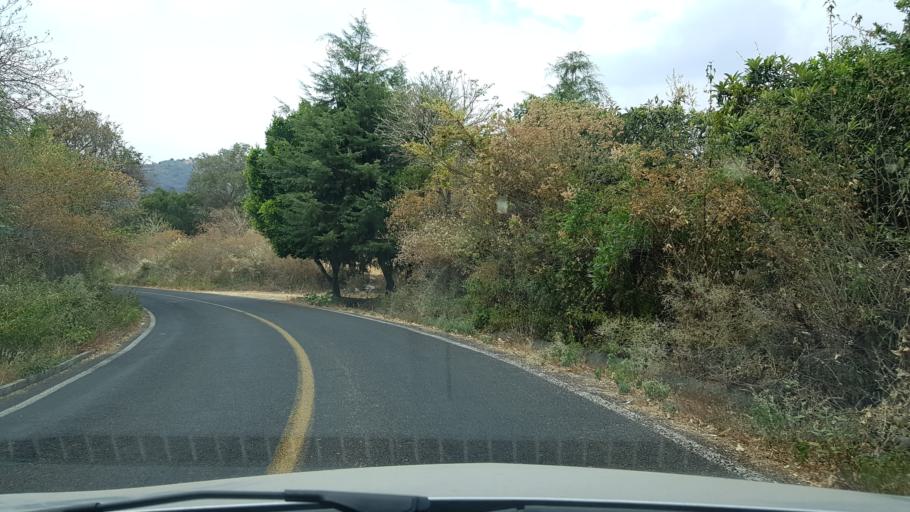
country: MX
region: Morelos
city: Tlacotepec
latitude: 18.8372
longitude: -98.7274
